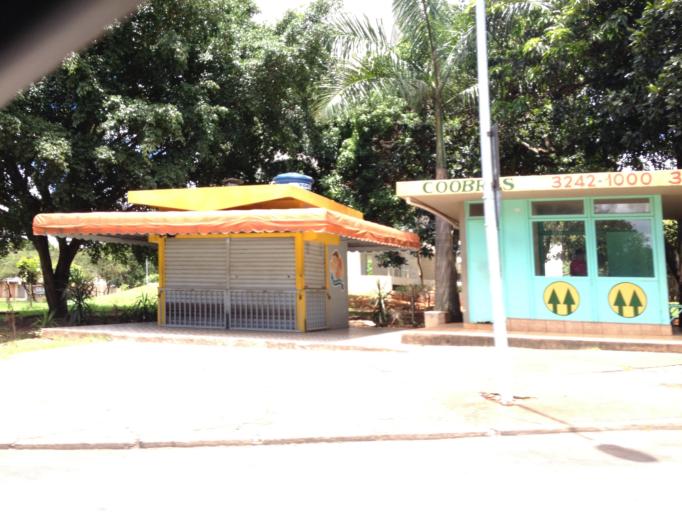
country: BR
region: Federal District
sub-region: Brasilia
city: Brasilia
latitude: -15.8178
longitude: -47.9079
